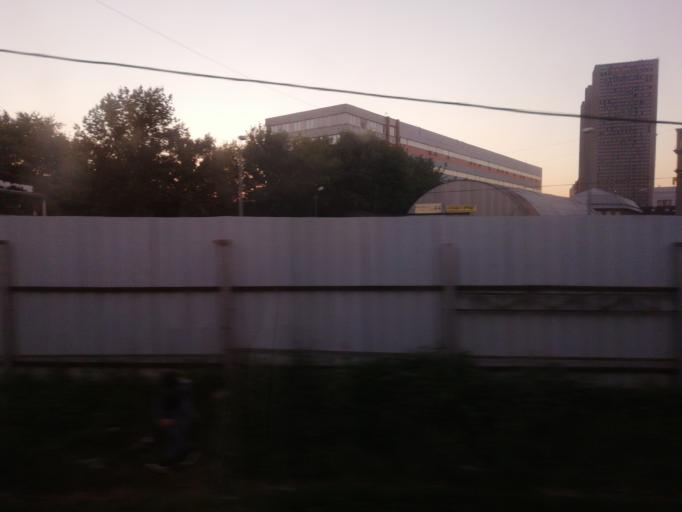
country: RU
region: Moscow
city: Mar'ina Roshcha
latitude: 55.7978
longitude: 37.5944
